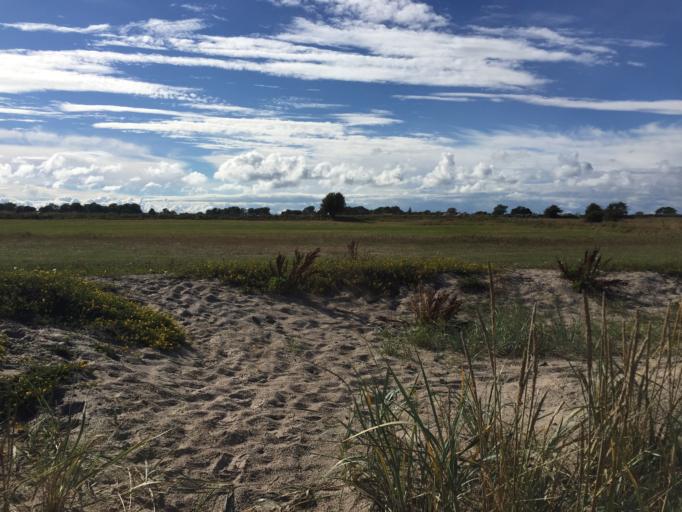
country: SE
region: Kalmar
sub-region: Morbylanga Kommun
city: Moerbylanga
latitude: 56.2510
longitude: 16.4847
